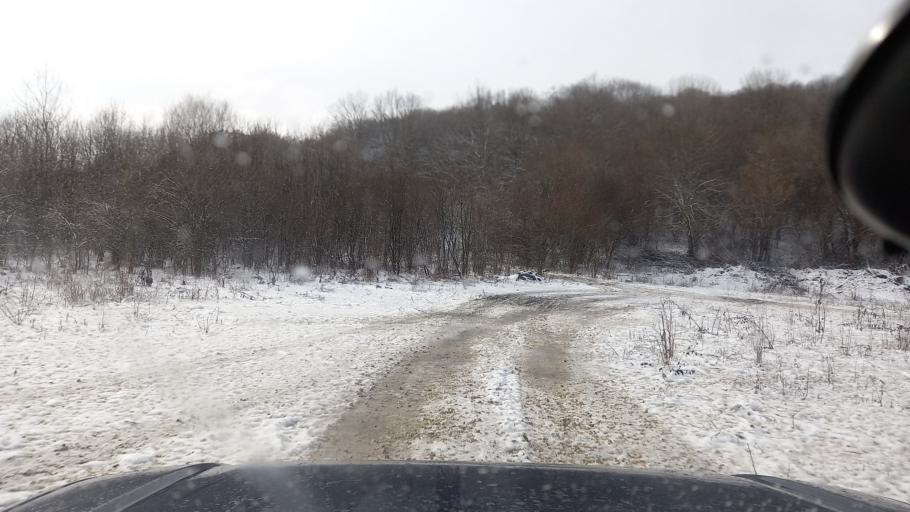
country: RU
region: Adygeya
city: Kamennomostskiy
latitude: 44.2450
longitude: 40.1976
